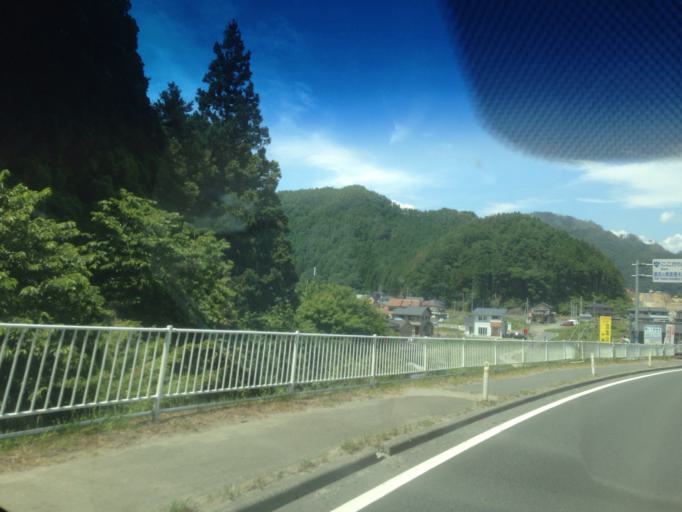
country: JP
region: Iwate
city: Kamaishi
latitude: 39.3203
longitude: 141.8835
